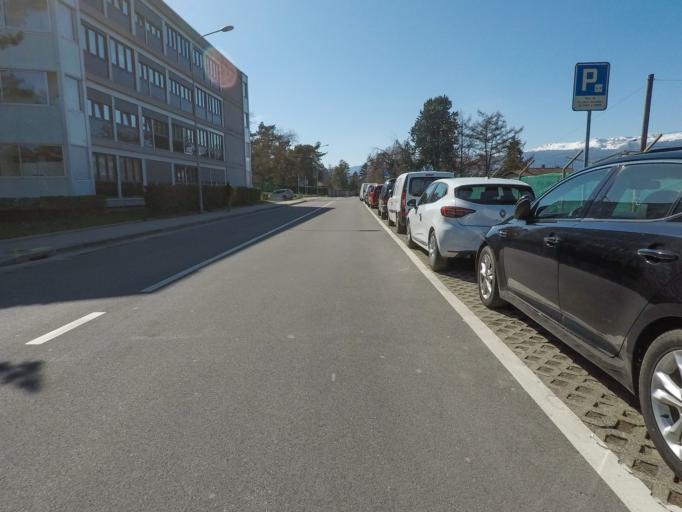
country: CH
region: Geneva
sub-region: Geneva
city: Vernier
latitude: 46.2170
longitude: 6.0825
